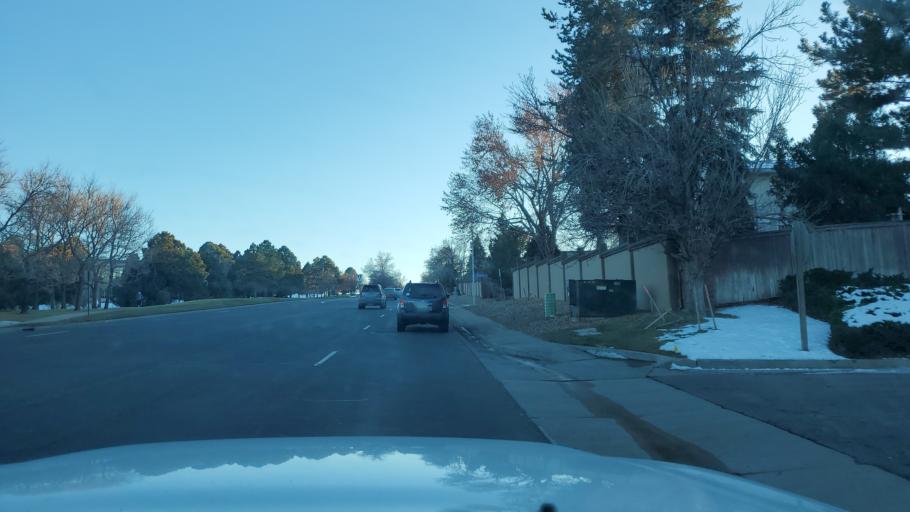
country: US
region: Colorado
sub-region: Arapahoe County
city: Castlewood
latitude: 39.6061
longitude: -104.9042
